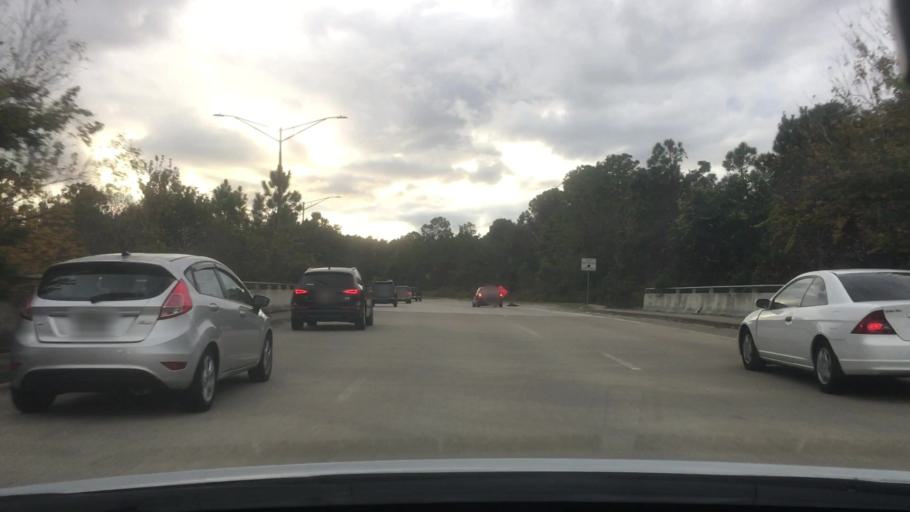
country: US
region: Florida
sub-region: Duval County
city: Jacksonville Beach
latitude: 30.2672
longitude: -81.5255
